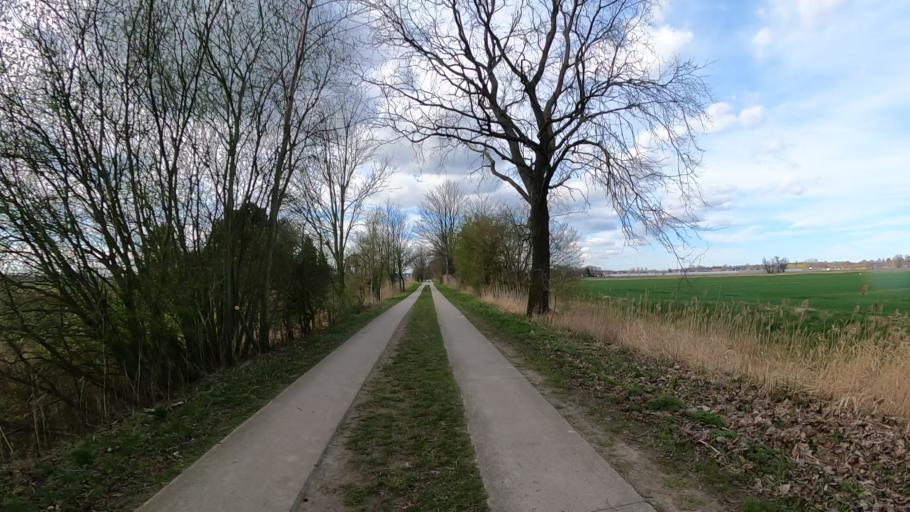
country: DE
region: Hamburg
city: Rothenburgsort
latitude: 53.4686
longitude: 10.0925
